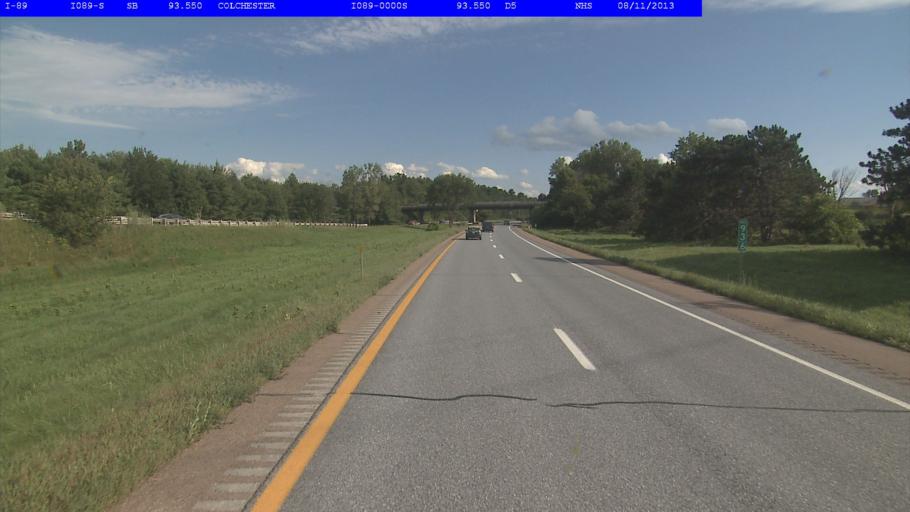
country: US
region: Vermont
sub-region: Chittenden County
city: Winooski
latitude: 44.5320
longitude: -73.1963
